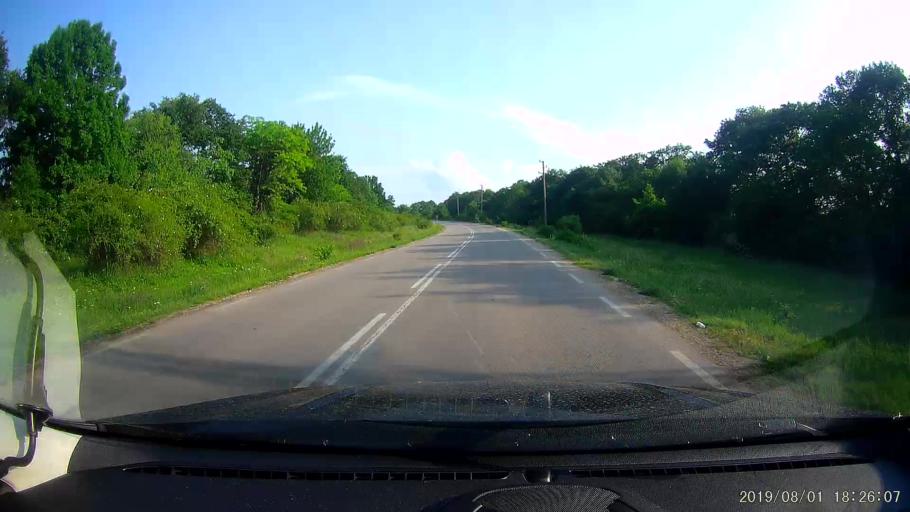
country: BG
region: Shumen
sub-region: Obshtina Venets
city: Venets
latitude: 43.6065
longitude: 26.9946
